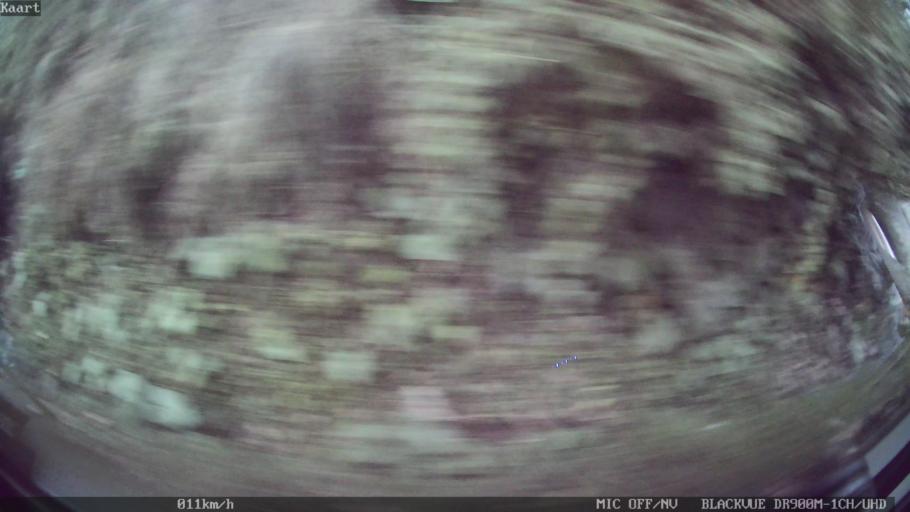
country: ID
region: Bali
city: Empalan
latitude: -8.3821
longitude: 115.1496
